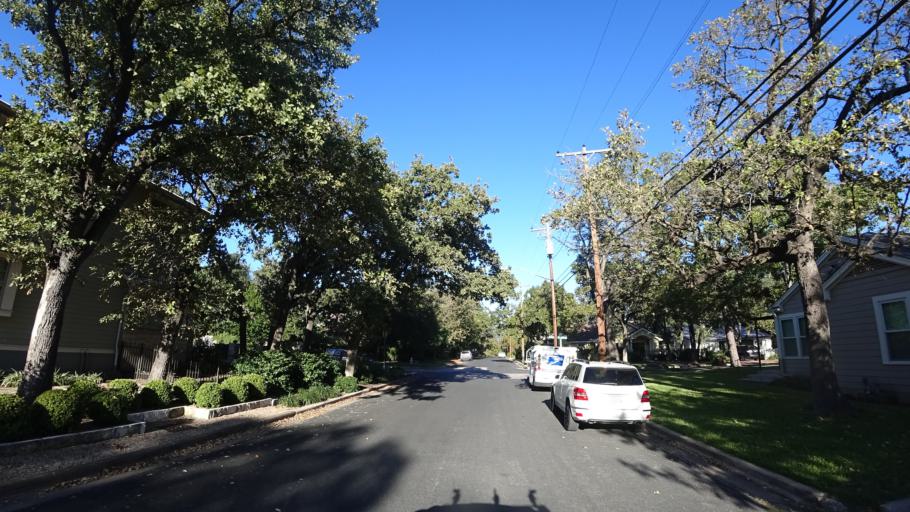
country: US
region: Texas
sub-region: Travis County
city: Rollingwood
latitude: 30.2966
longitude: -97.7703
